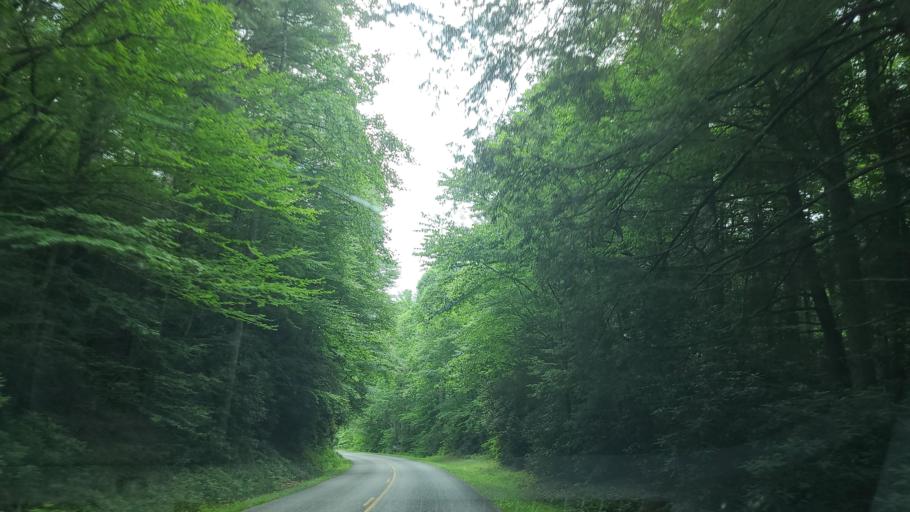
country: US
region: North Carolina
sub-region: Avery County
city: Newland
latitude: 35.9860
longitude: -81.9001
